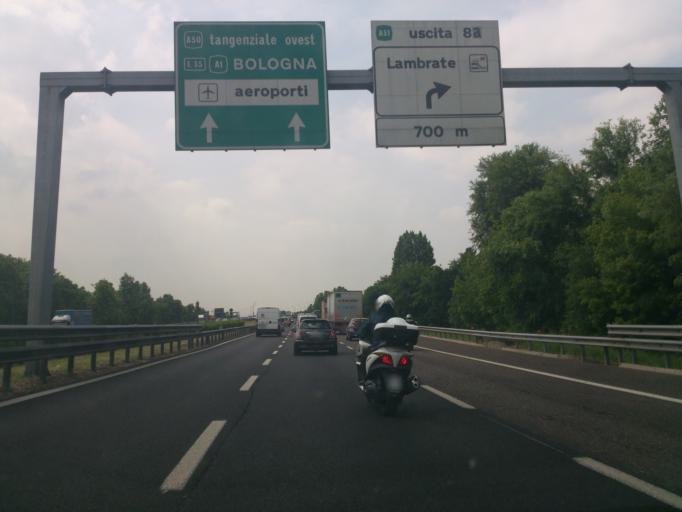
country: IT
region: Lombardy
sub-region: Citta metropolitana di Milano
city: Vimodrone
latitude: 45.4957
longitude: 9.2546
